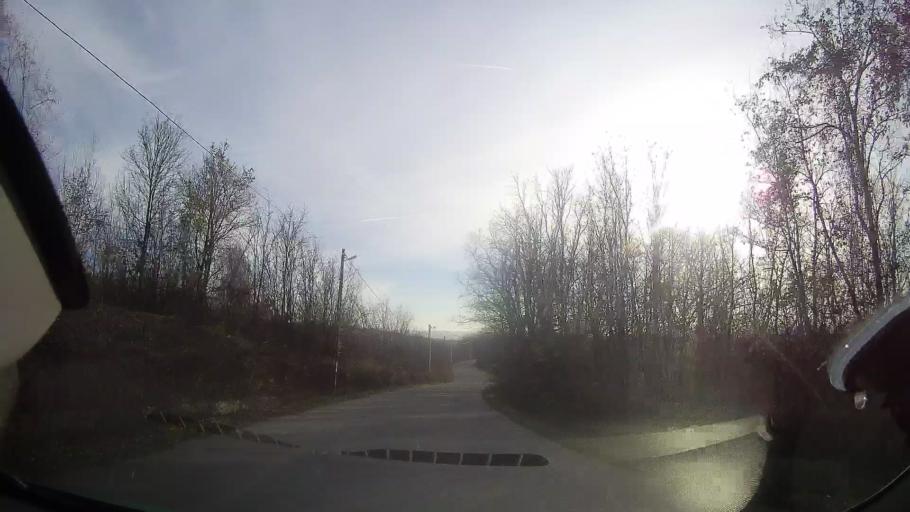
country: RO
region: Bihor
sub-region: Comuna Sarbi
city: Burzuc
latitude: 47.1160
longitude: 22.1793
